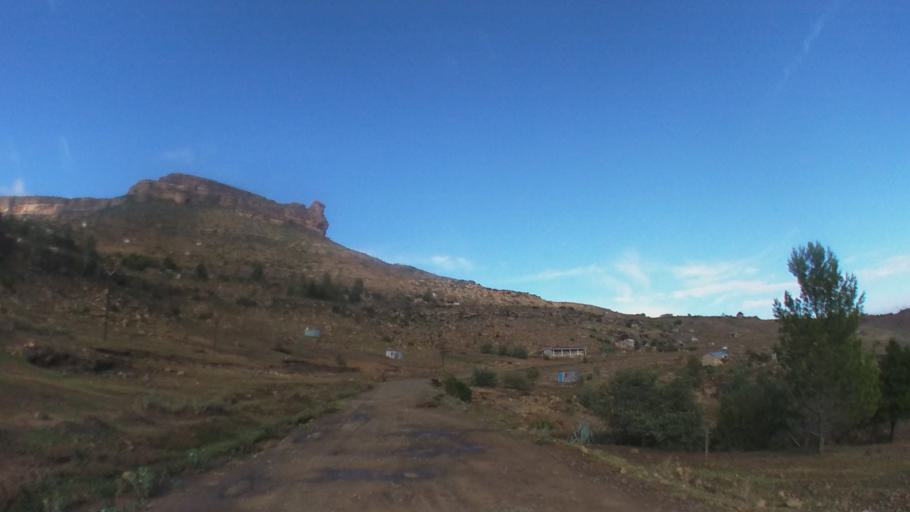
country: LS
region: Maseru
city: Maseru
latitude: -29.4050
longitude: 27.4692
